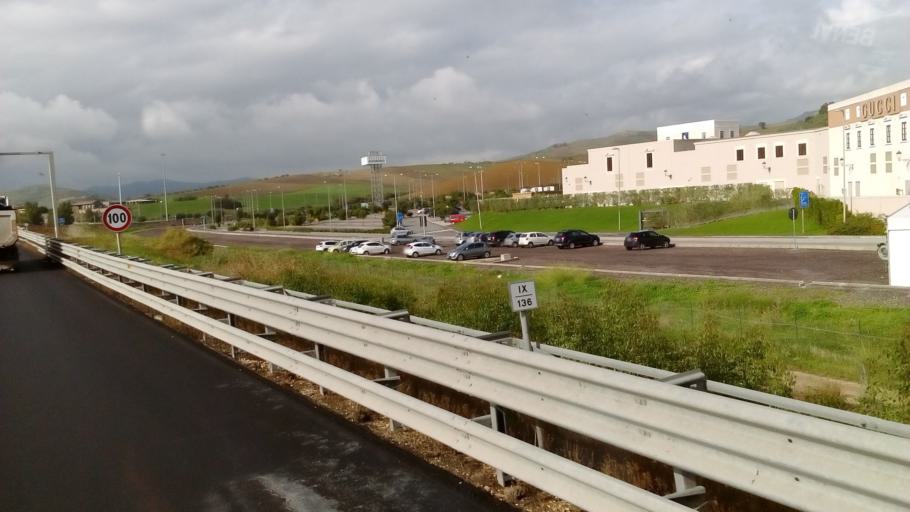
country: IT
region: Sicily
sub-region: Enna
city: Assoro
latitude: 37.5710
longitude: 14.4819
